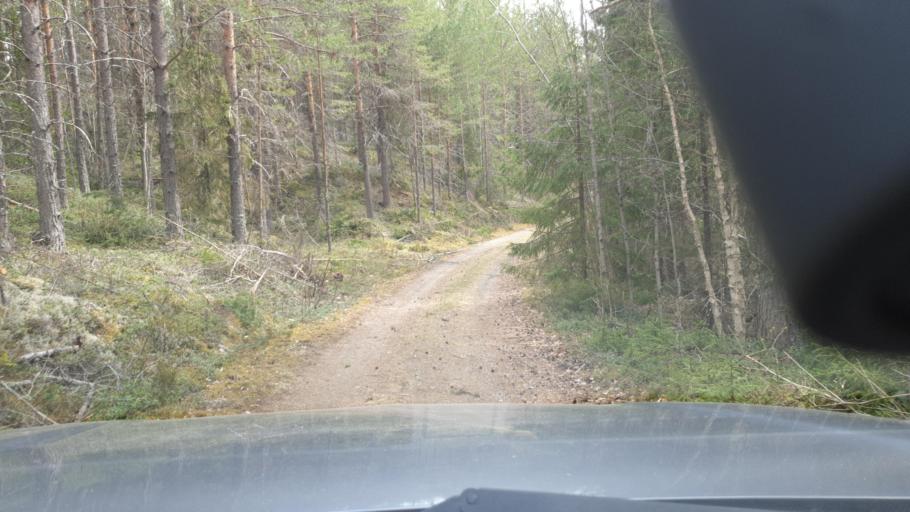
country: SE
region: Vaesternorrland
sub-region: Ange Kommun
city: Ange
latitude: 62.1868
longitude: 15.6169
